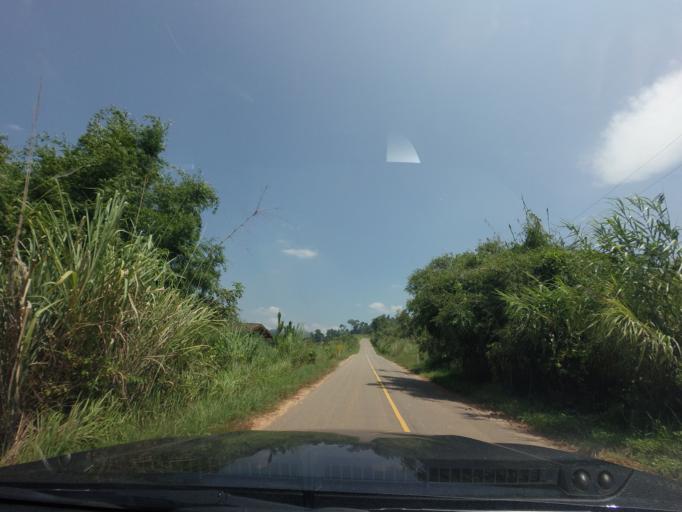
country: TH
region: Loei
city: Na Haeo
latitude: 17.5668
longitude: 100.8912
